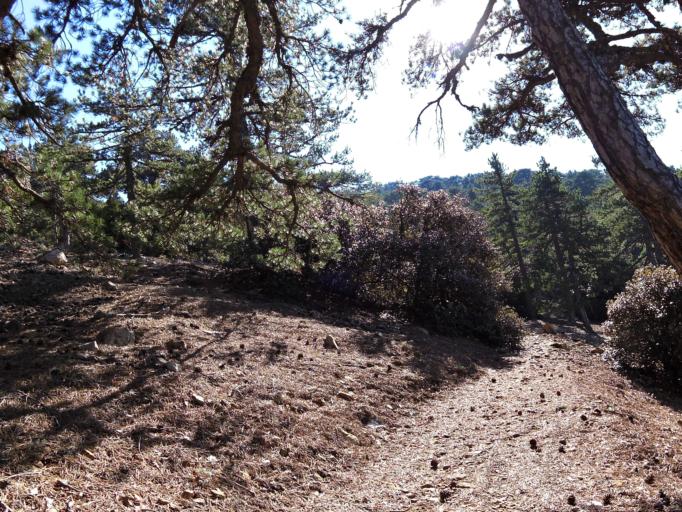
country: CY
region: Lefkosia
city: Kakopetria
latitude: 34.9571
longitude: 32.8529
